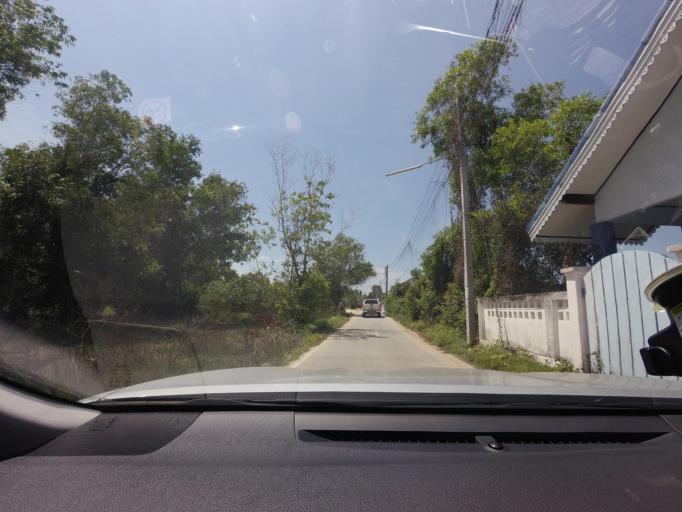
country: TH
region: Narathiwat
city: Narathiwat
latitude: 6.4433
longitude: 101.8096
